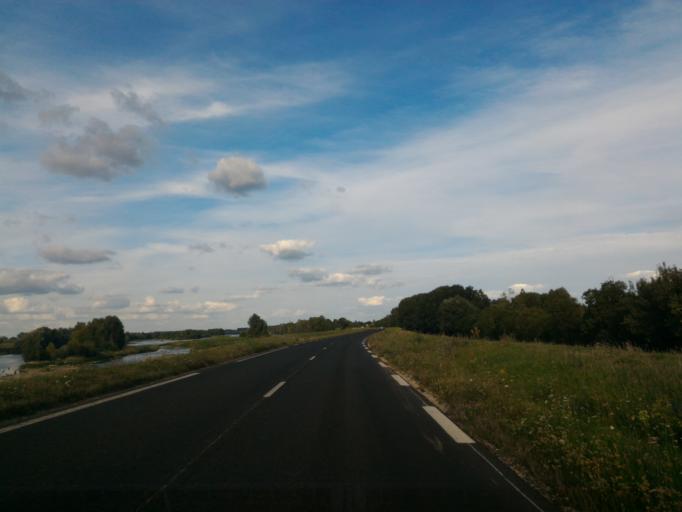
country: FR
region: Centre
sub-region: Departement du Loir-et-Cher
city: Suevres
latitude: 47.6518
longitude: 1.4603
